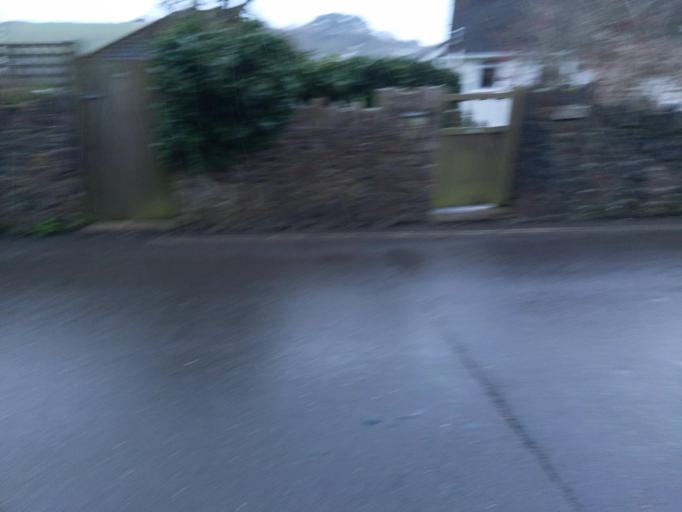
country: GB
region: England
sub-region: Devon
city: Wembury
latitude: 50.3152
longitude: -4.0378
